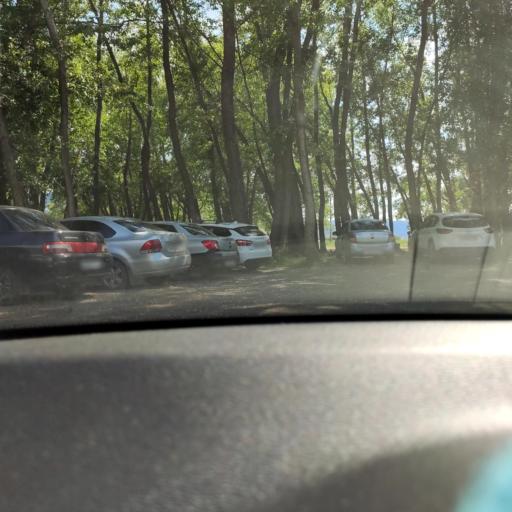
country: RU
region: Samara
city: Volzhskiy
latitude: 53.4322
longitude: 50.1666
